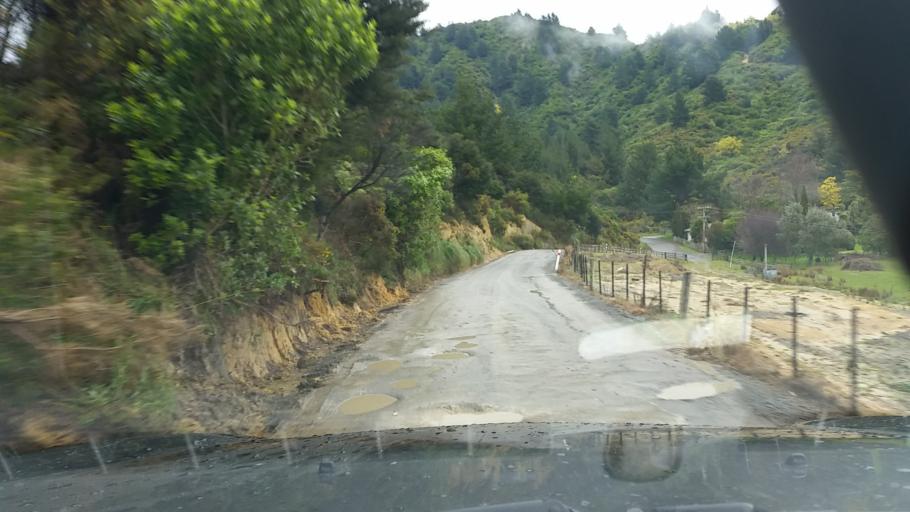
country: NZ
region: Marlborough
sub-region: Marlborough District
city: Picton
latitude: -41.2795
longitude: 174.0320
